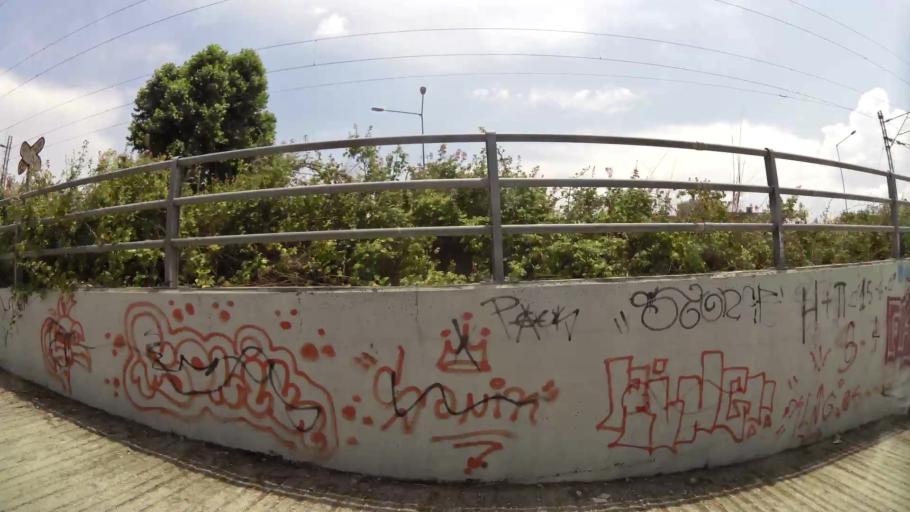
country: GR
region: Central Macedonia
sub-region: Nomos Pierias
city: Peristasi
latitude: 40.2778
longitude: 22.5407
